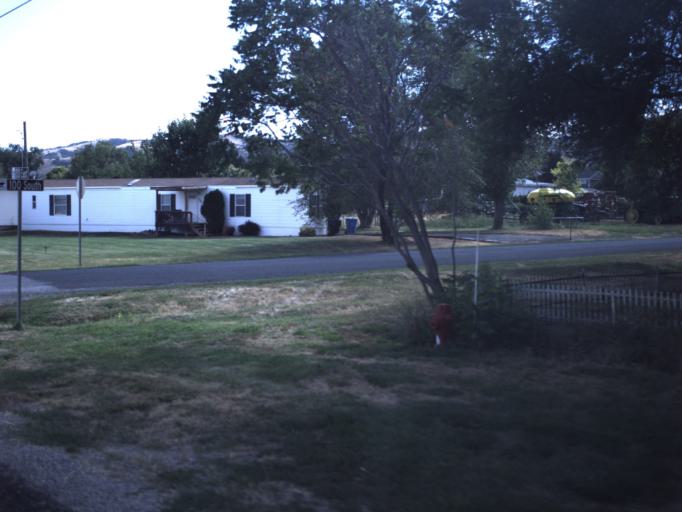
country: US
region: Utah
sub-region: Cache County
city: Benson
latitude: 41.9181
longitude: -112.0451
